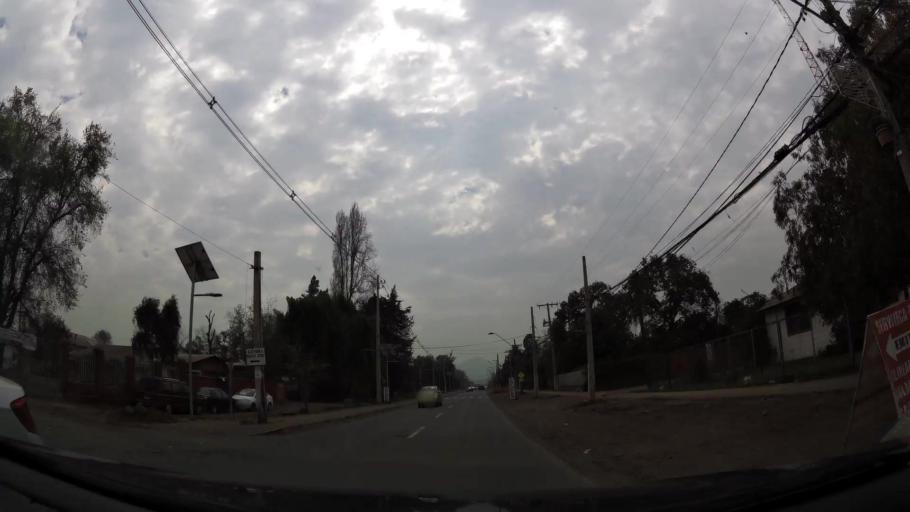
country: CL
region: Santiago Metropolitan
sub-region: Provincia de Chacabuco
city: Chicureo Abajo
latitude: -33.1981
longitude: -70.6785
